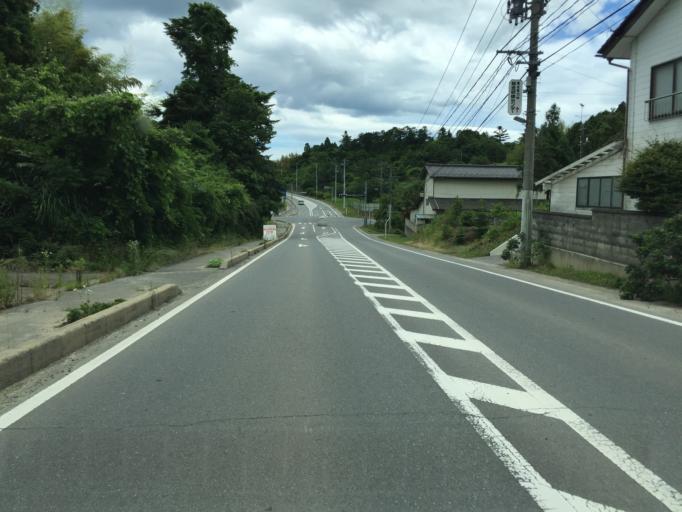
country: JP
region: Fukushima
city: Namie
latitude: 37.6524
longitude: 141.0116
